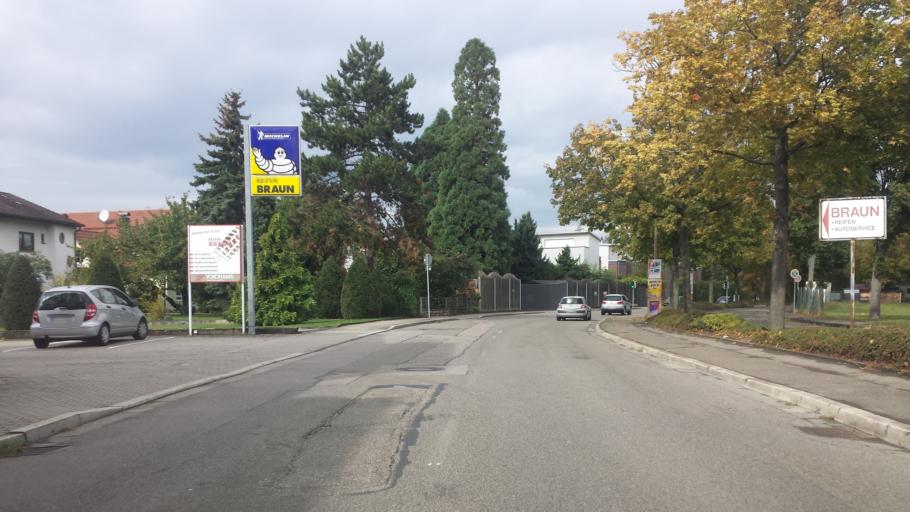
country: DE
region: Baden-Wuerttemberg
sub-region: Karlsruhe Region
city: Bruchsal
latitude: 49.1292
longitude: 8.5816
